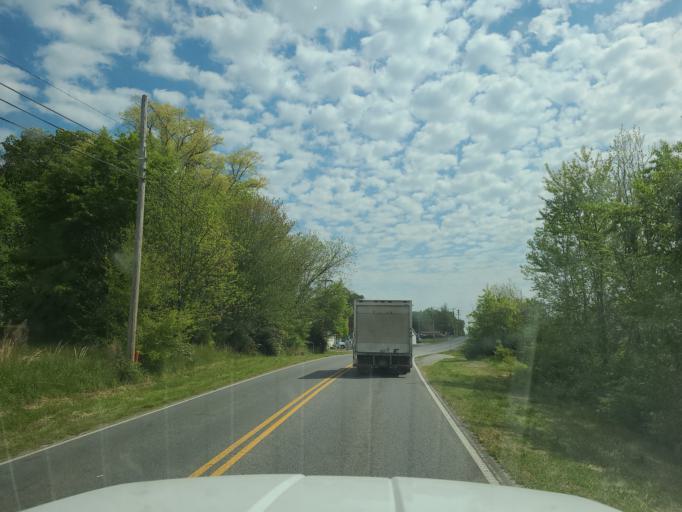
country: US
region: North Carolina
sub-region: Gaston County
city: Cherryville
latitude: 35.3609
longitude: -81.4309
